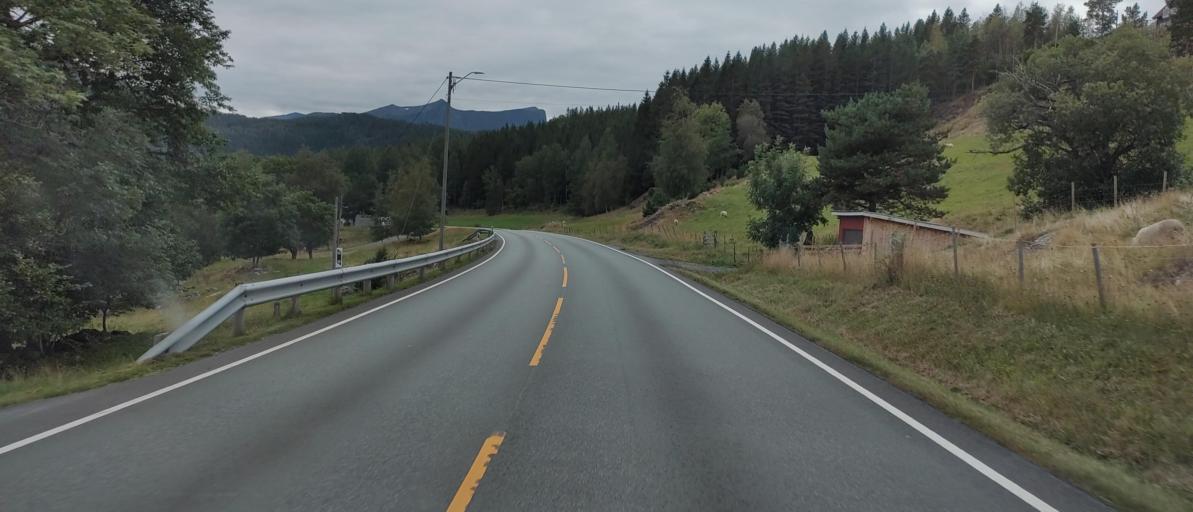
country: NO
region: More og Romsdal
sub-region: Rauma
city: Andalsnes
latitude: 62.5805
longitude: 7.5551
